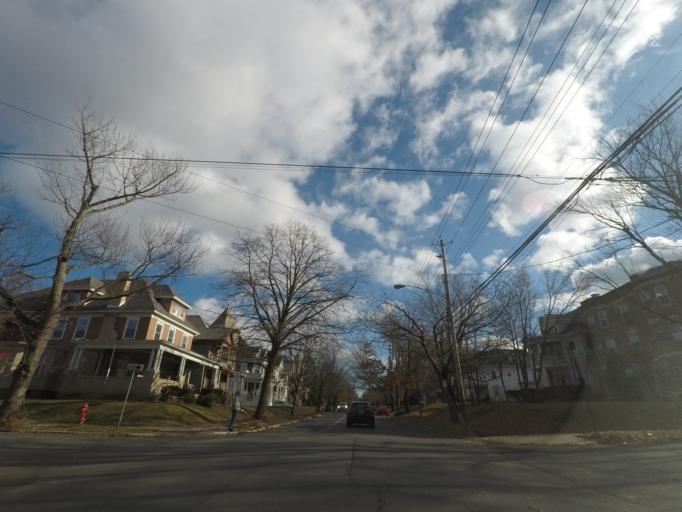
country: US
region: New York
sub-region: Schenectady County
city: Schenectady
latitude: 42.8127
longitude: -73.9260
